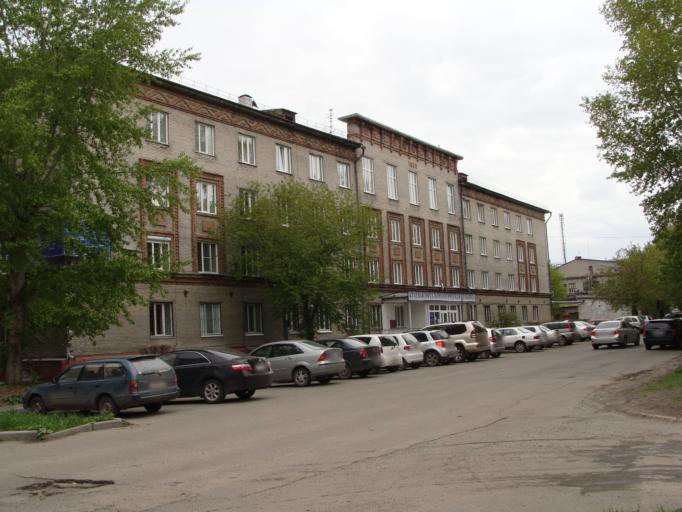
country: RU
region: Altai Krai
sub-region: Gorod Barnaulskiy
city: Barnaul
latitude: 53.3547
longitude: 83.7751
